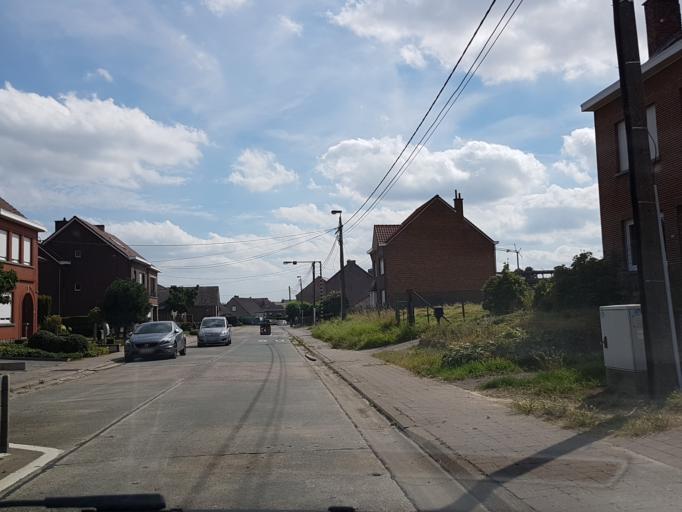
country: BE
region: Flanders
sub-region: Provincie Vlaams-Brabant
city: Bertem
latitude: 50.8729
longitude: 4.6297
